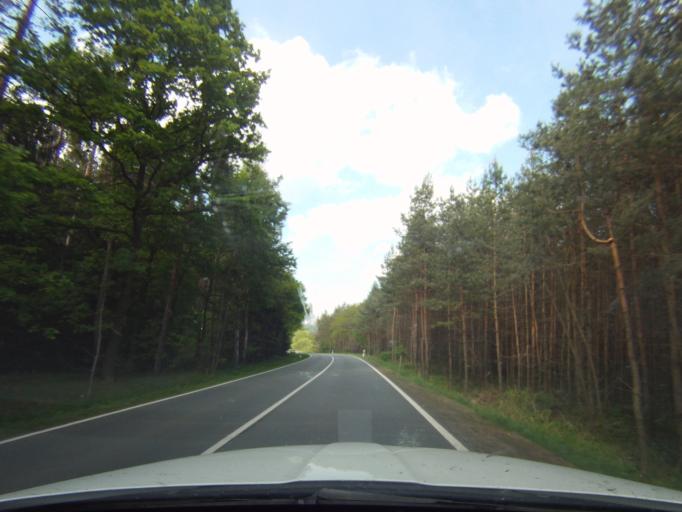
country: DE
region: Thuringia
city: Mittelpollnitz
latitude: 50.7728
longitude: 11.9332
